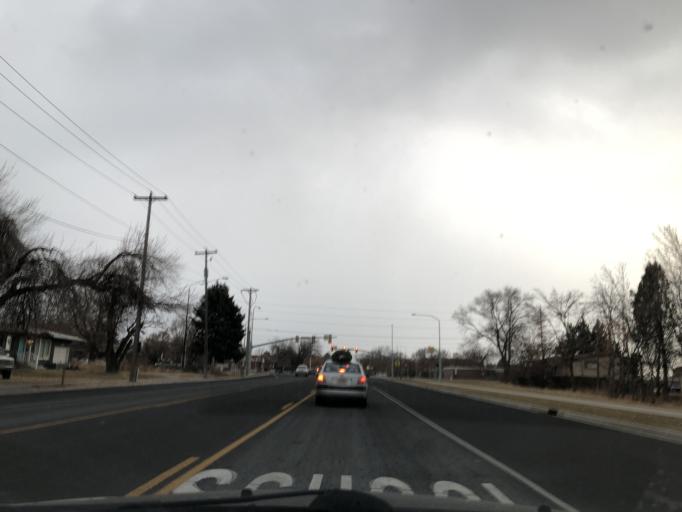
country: US
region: Utah
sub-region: Cache County
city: Logan
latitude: 41.7513
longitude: -111.8294
